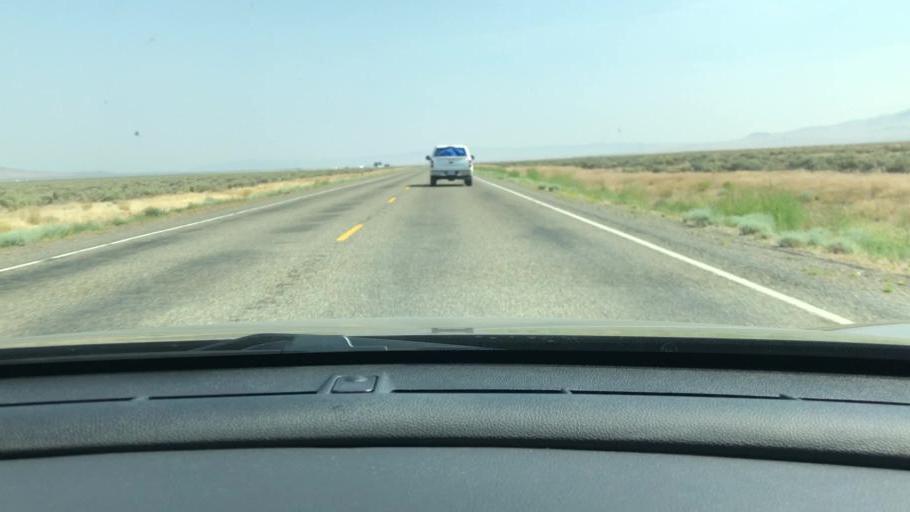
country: US
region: Nevada
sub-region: Humboldt County
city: Winnemucca
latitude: 41.7553
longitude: -117.7550
